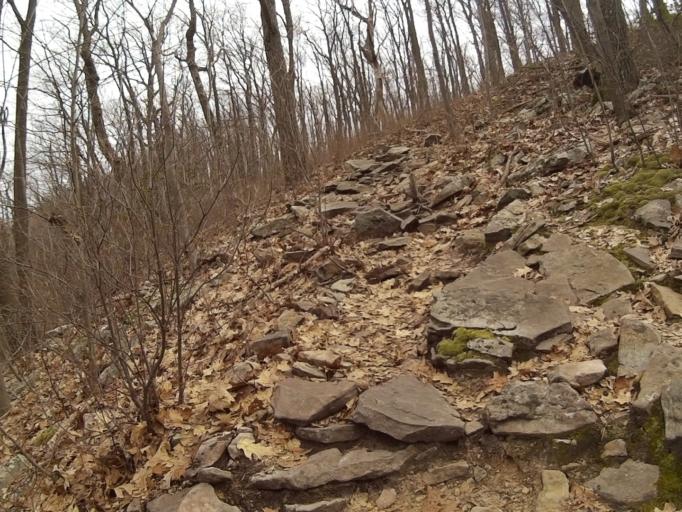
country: US
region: Pennsylvania
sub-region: Centre County
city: Lemont
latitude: 40.8173
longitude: -77.7922
